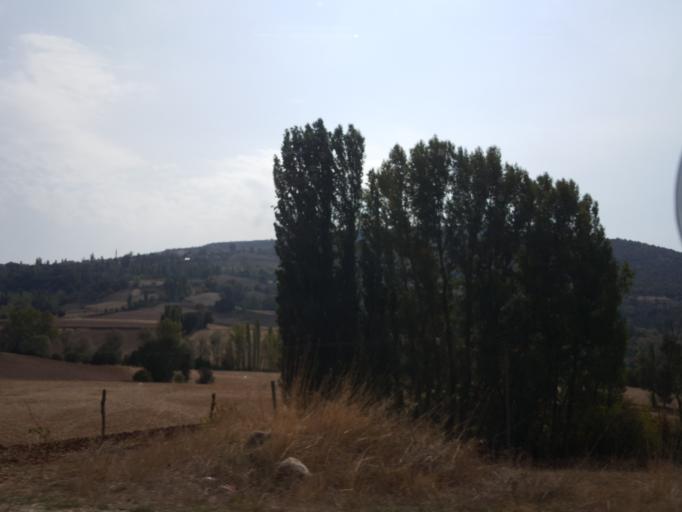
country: TR
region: Tokat
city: Zile
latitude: 40.3673
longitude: 35.8562
